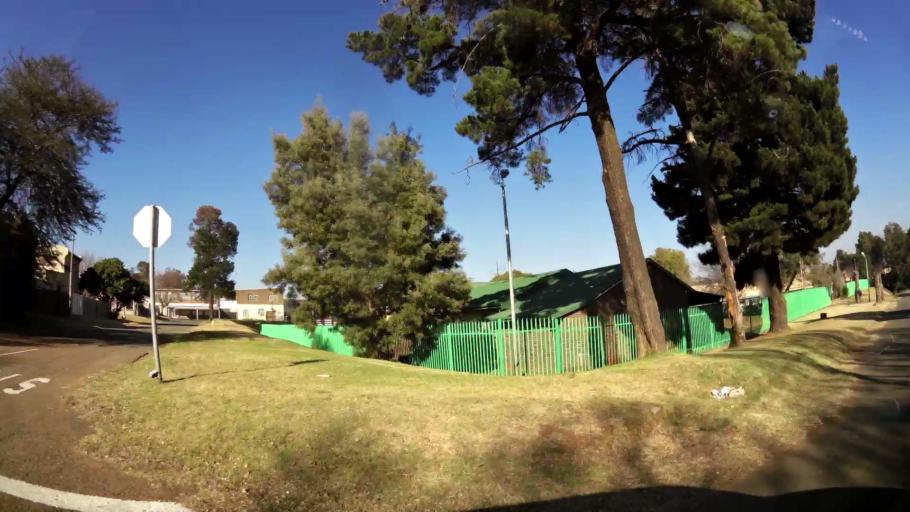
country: ZA
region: Gauteng
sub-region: City of Johannesburg Metropolitan Municipality
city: Roodepoort
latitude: -26.1608
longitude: 27.8593
